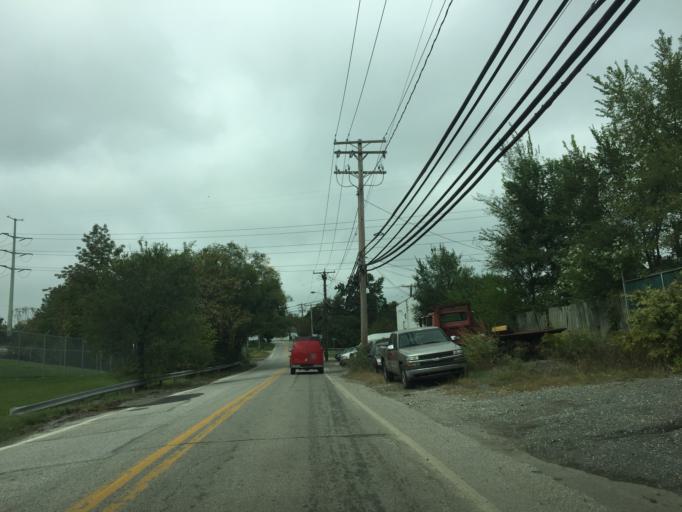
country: US
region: Maryland
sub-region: Baltimore County
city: Rossville
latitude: 39.3299
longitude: -76.4757
